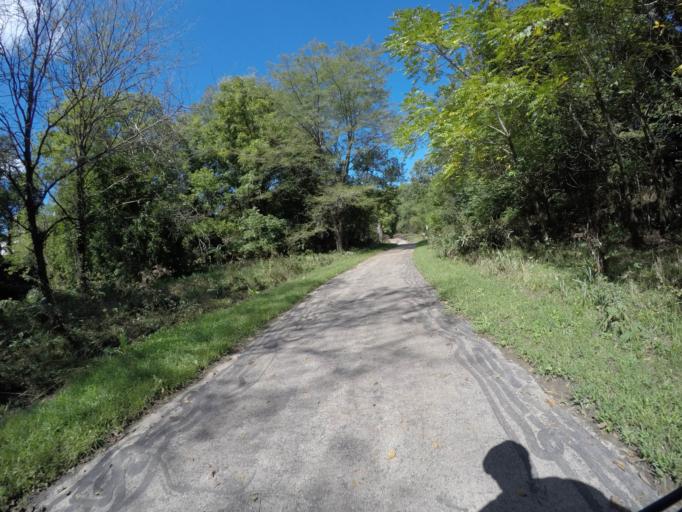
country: US
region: Kansas
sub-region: Johnson County
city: Lenexa
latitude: 38.8990
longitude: -94.7519
